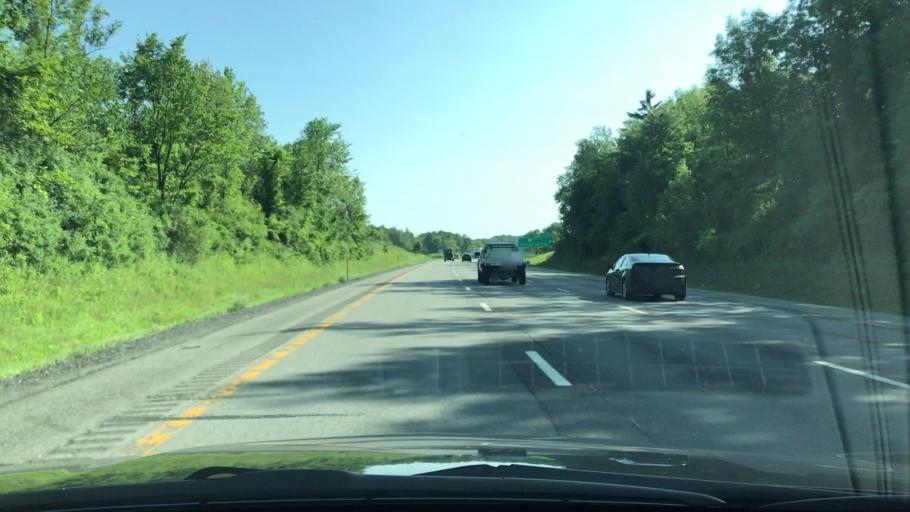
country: US
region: New York
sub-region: Saratoga County
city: Saratoga Springs
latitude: 43.0293
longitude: -73.7841
